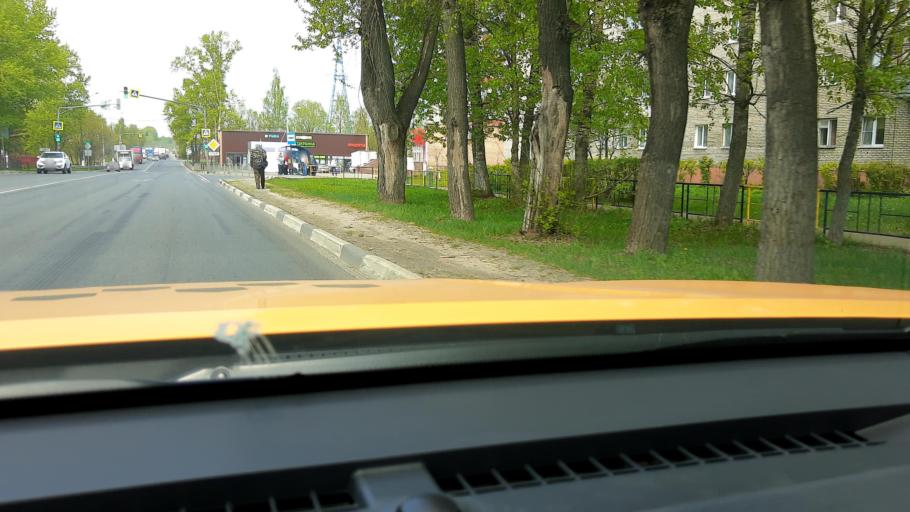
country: RU
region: Moskovskaya
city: Noginsk
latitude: 55.8784
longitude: 38.4302
